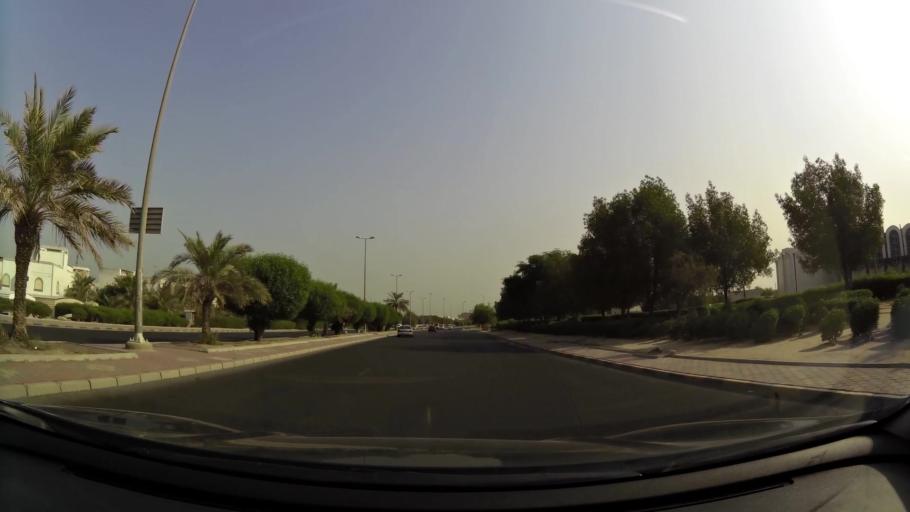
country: KW
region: Mubarak al Kabir
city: Sabah as Salim
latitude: 29.2507
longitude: 48.0661
